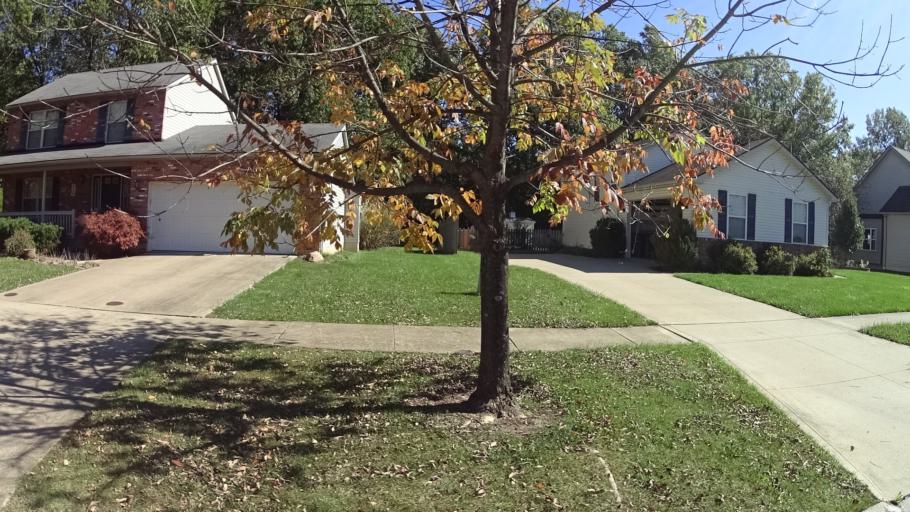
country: US
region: Ohio
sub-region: Lorain County
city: Oberlin
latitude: 41.3000
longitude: -82.2295
